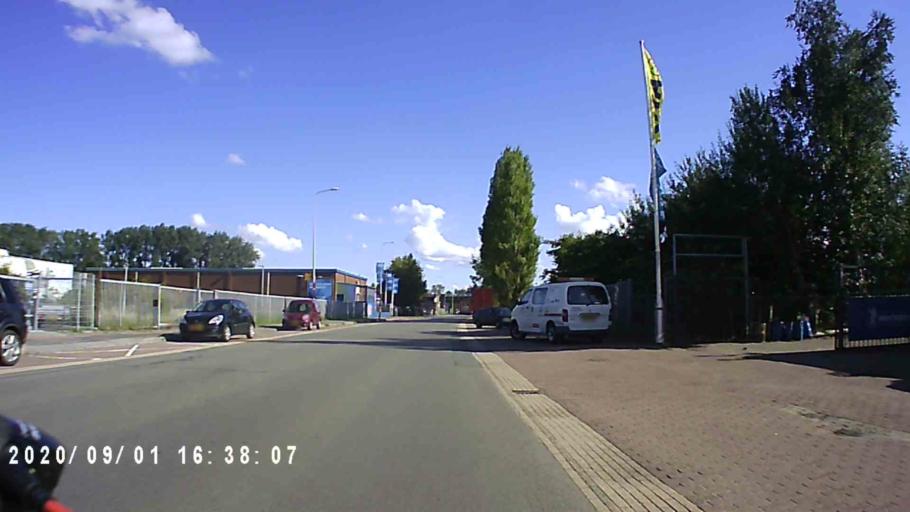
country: NL
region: Groningen
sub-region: Gemeente Groningen
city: Oosterpark
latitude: 53.2356
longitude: 6.5840
